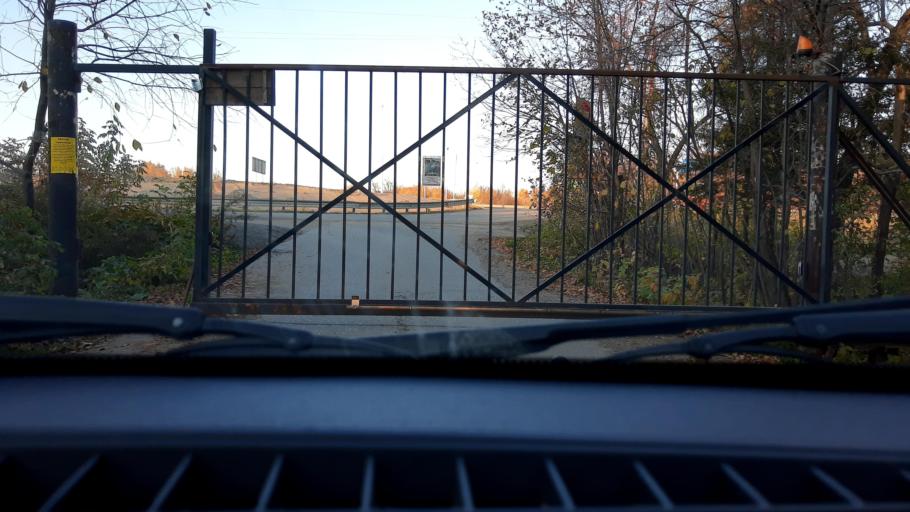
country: RU
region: Bashkortostan
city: Ufa
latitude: 54.6795
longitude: 56.0078
